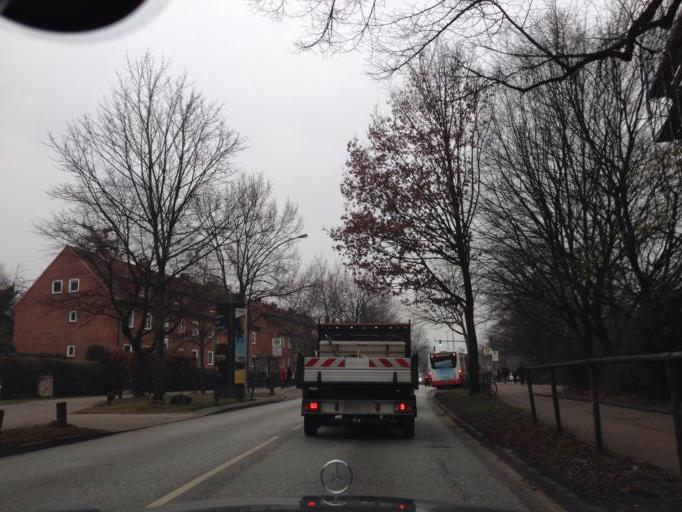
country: DE
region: Hamburg
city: Farmsen-Berne
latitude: 53.6033
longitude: 10.1273
